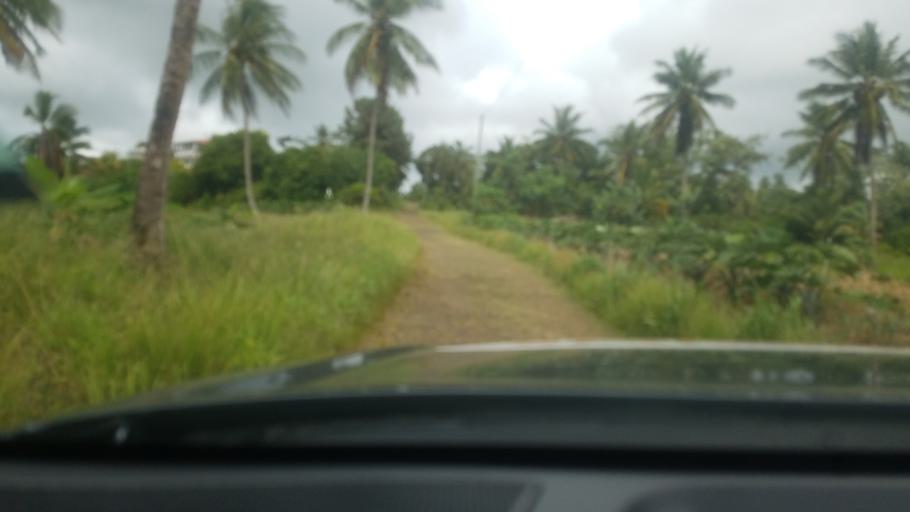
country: LC
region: Micoud Quarter
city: Micoud
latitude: 13.8052
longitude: -60.9398
